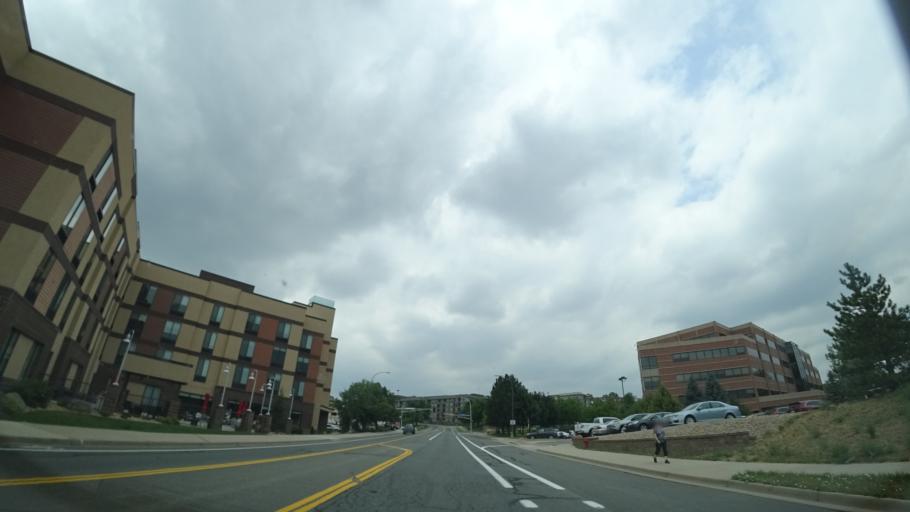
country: US
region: Colorado
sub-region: Jefferson County
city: West Pleasant View
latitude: 39.7170
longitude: -105.1360
